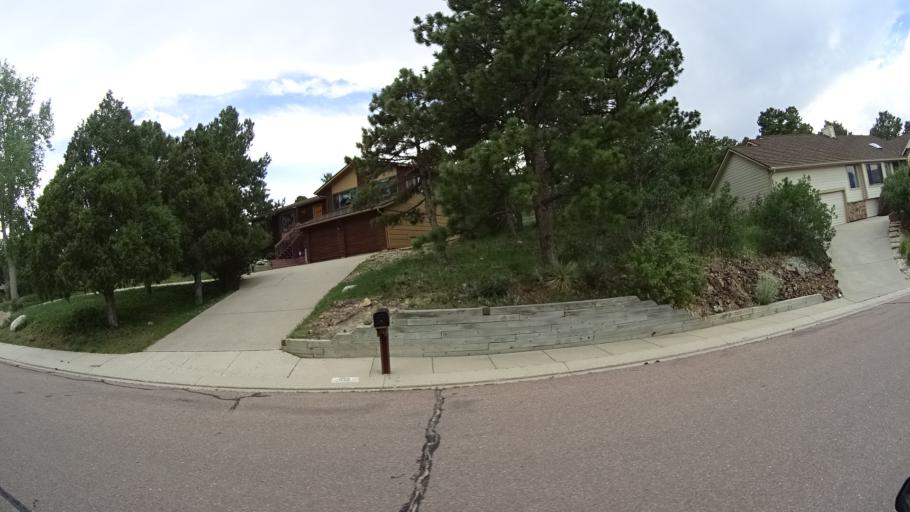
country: US
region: Colorado
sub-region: El Paso County
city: Colorado Springs
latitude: 38.9075
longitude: -104.8425
